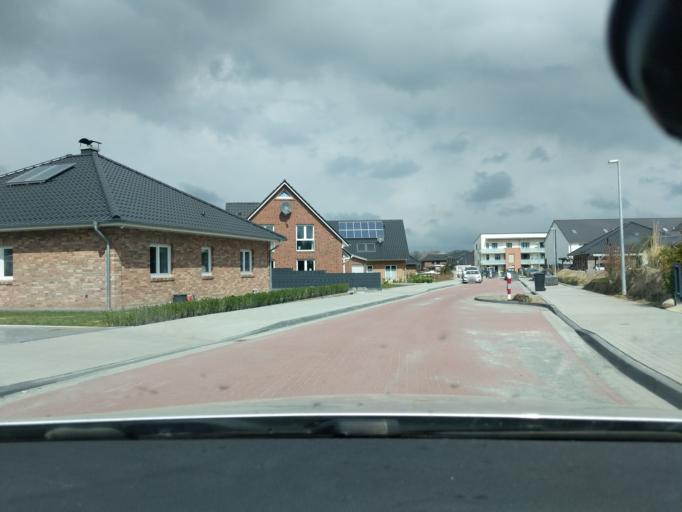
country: DE
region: Lower Saxony
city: Stade
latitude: 53.5680
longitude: 9.4664
